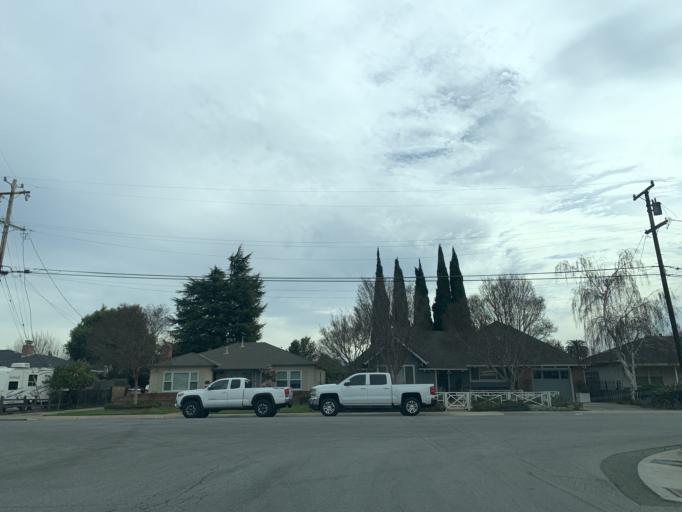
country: US
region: California
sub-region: Santa Clara County
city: Buena Vista
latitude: 37.3141
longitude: -121.9197
